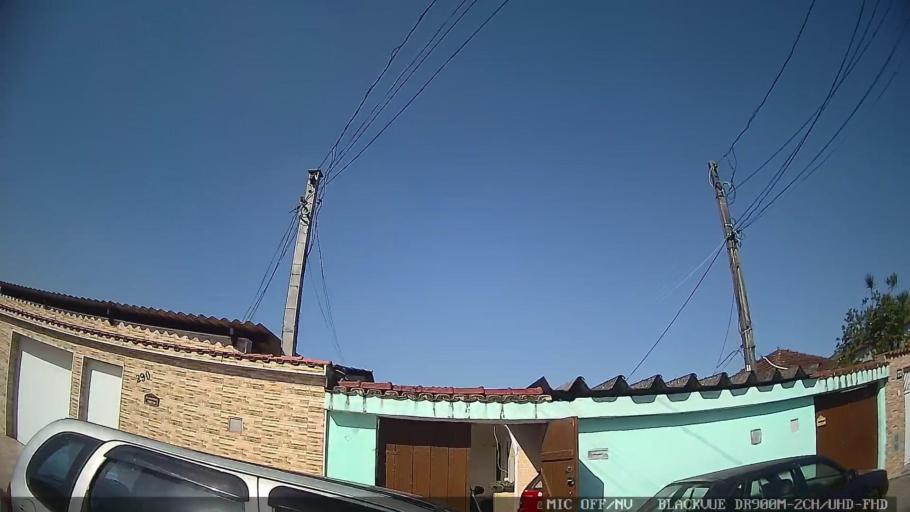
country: BR
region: Sao Paulo
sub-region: Santos
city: Santos
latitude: -23.9442
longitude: -46.2955
